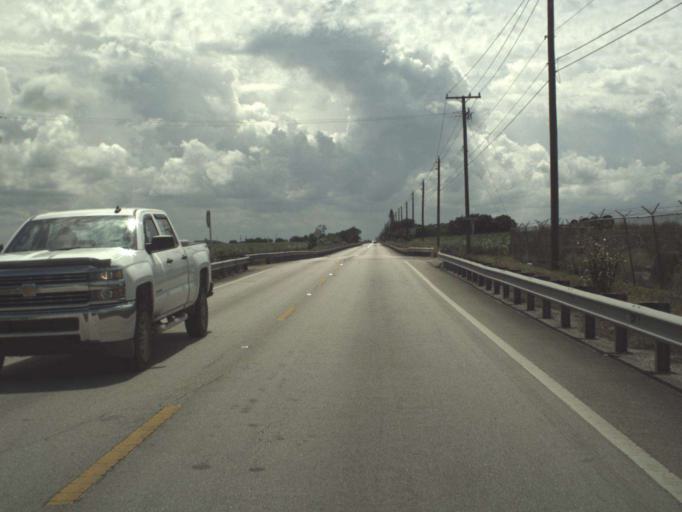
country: US
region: Florida
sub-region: Palm Beach County
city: Pahokee
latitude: 26.7990
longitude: -80.6534
